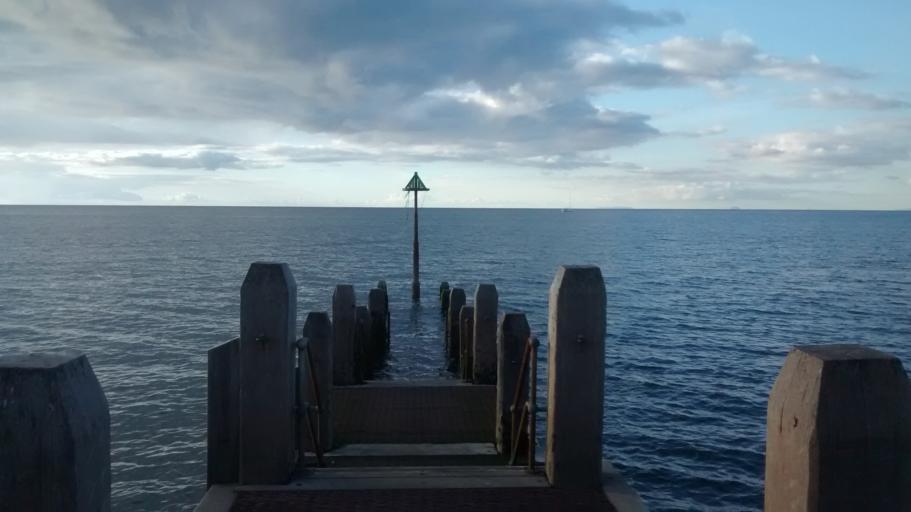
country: GB
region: Wales
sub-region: County of Ceredigion
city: Aberystwyth
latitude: 52.4167
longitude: -4.0860
